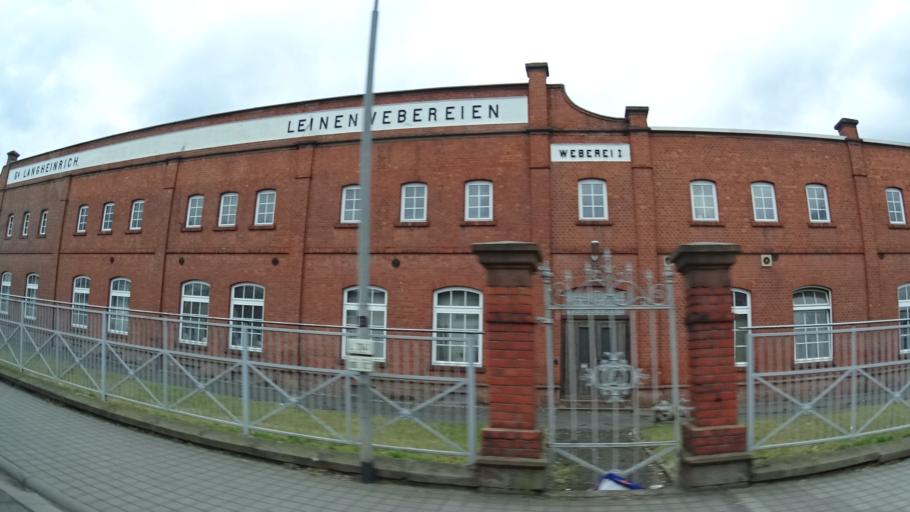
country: DE
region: Hesse
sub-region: Regierungsbezirk Giessen
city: Schlitz
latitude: 50.6774
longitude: 9.5626
